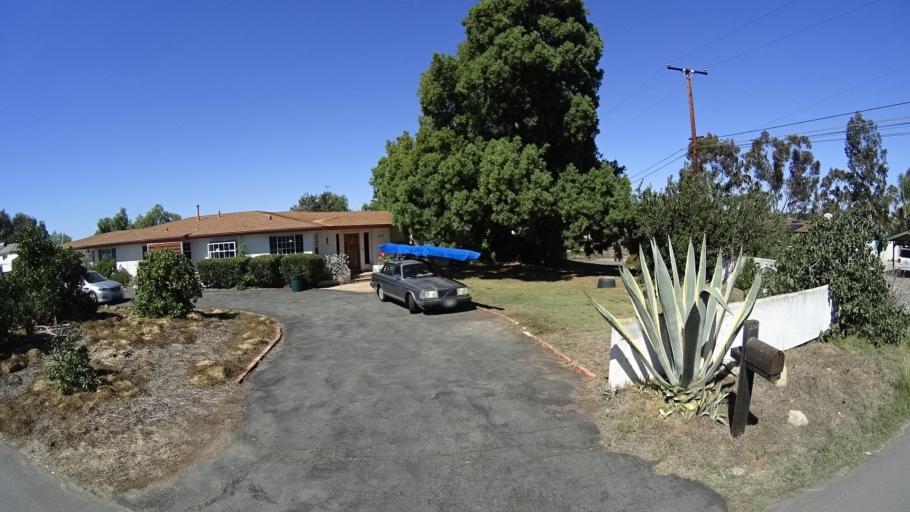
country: US
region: California
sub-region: San Diego County
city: Bonita
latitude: 32.6653
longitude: -117.0486
